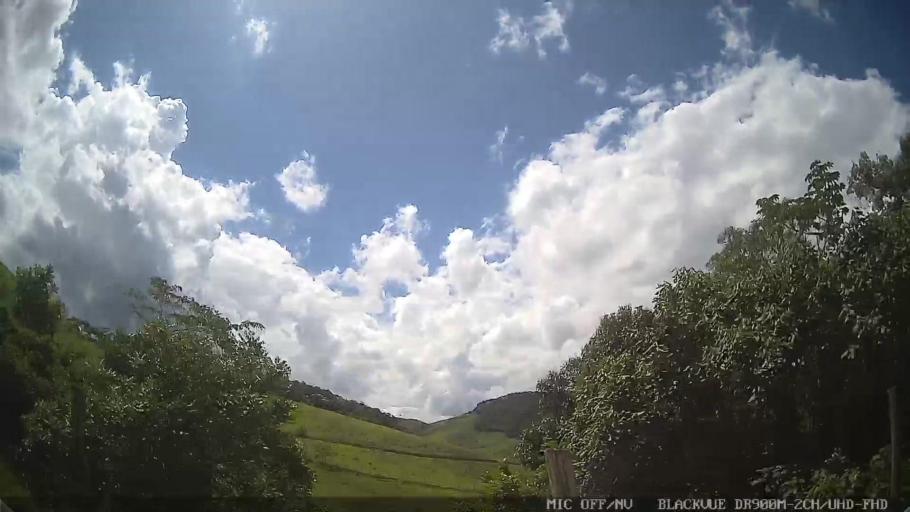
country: BR
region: Sao Paulo
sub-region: Caraguatatuba
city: Caraguatatuba
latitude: -23.5375
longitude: -45.5755
